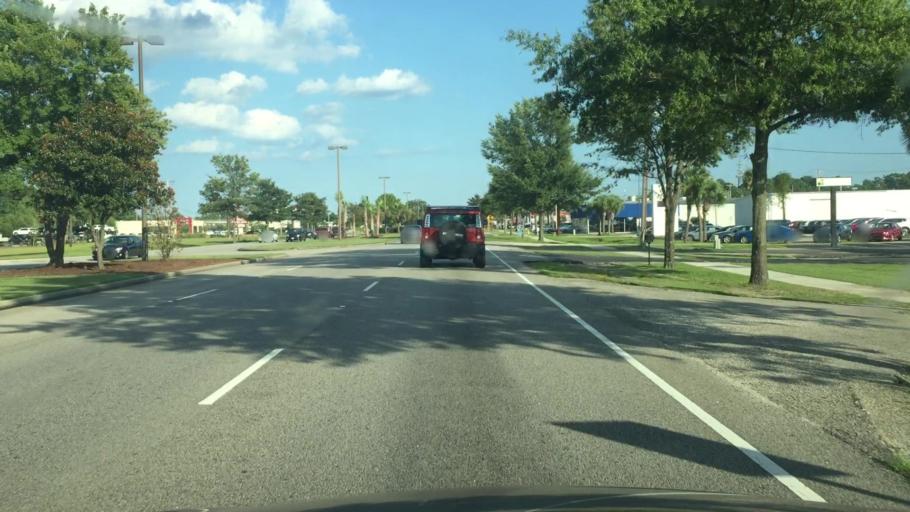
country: US
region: South Carolina
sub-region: Horry County
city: Myrtle Beach
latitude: 33.7045
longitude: -78.9079
